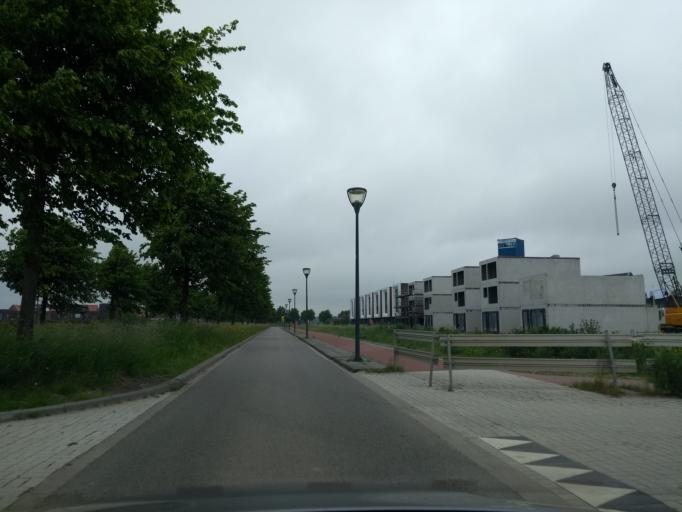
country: NL
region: Groningen
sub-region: Gemeente Groningen
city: Korrewegwijk
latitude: 53.2387
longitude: 6.5200
